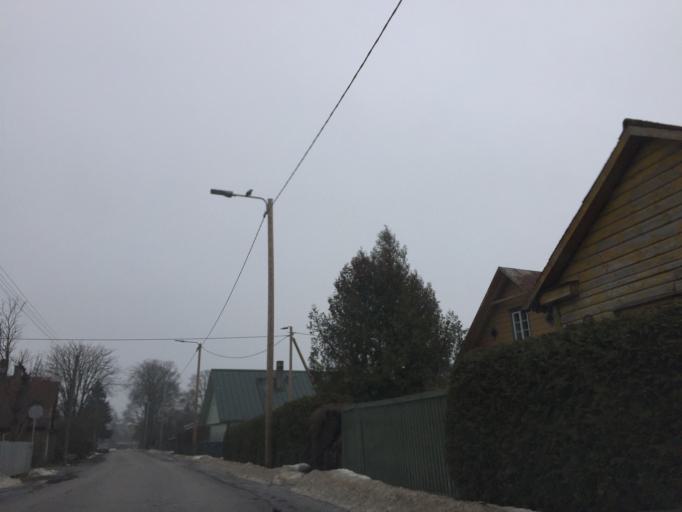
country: EE
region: Saare
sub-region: Kuressaare linn
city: Kuressaare
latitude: 58.2488
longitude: 22.4865
